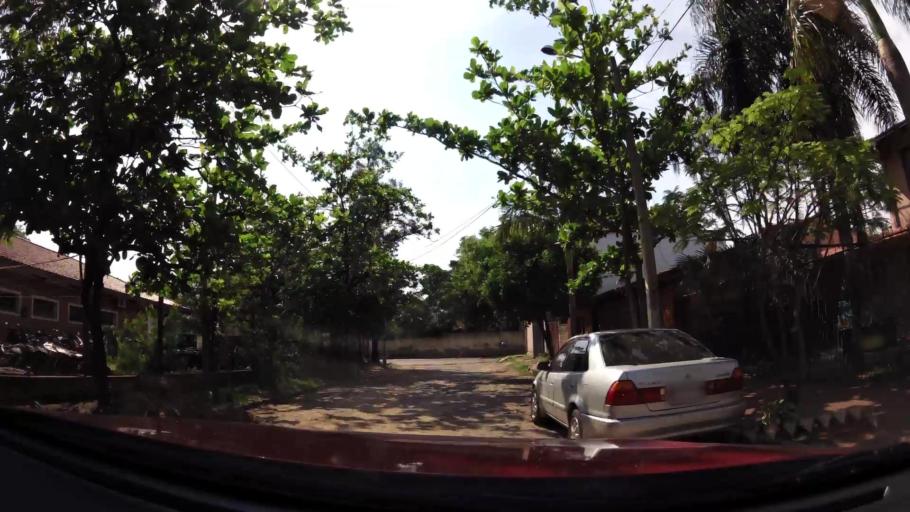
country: PY
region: Central
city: Fernando de la Mora
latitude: -25.2643
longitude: -57.5488
